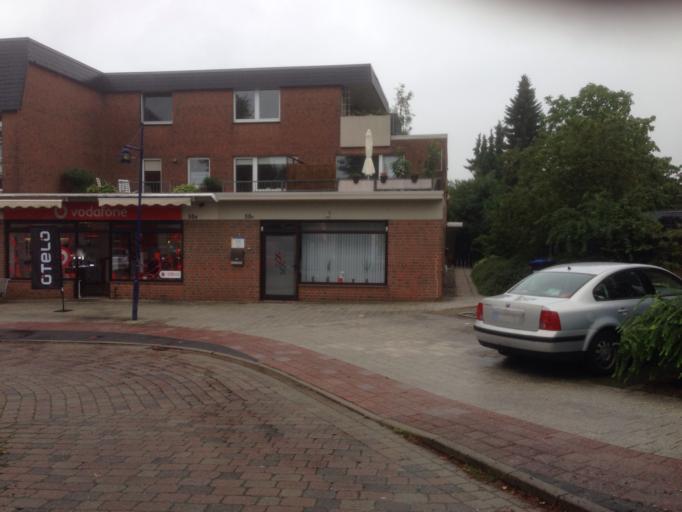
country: DE
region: Lower Saxony
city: Adendorf
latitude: 53.2808
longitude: 10.4381
